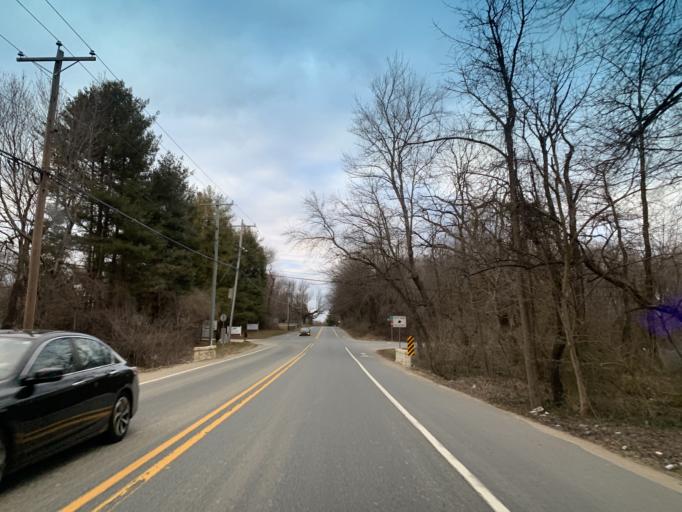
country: US
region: Delaware
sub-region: New Castle County
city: Bear
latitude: 39.5978
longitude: -75.6626
